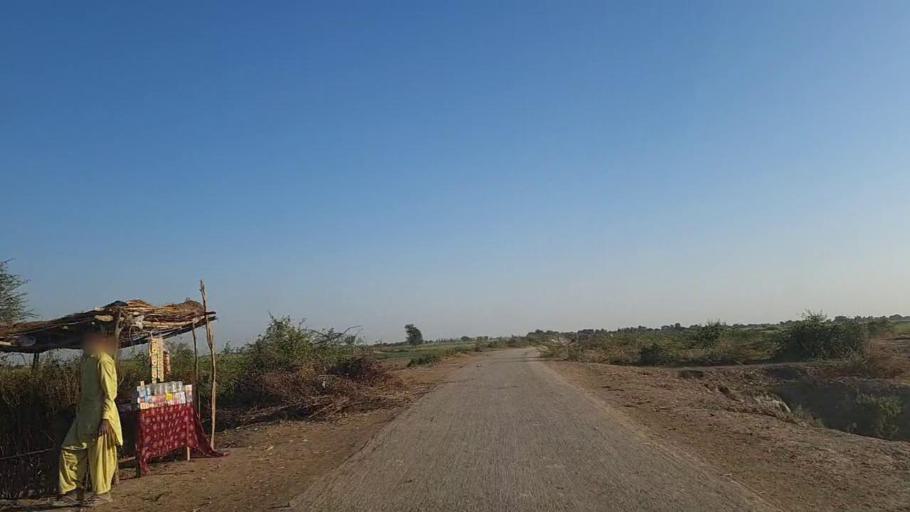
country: PK
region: Sindh
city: Naukot
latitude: 24.9867
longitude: 69.4042
